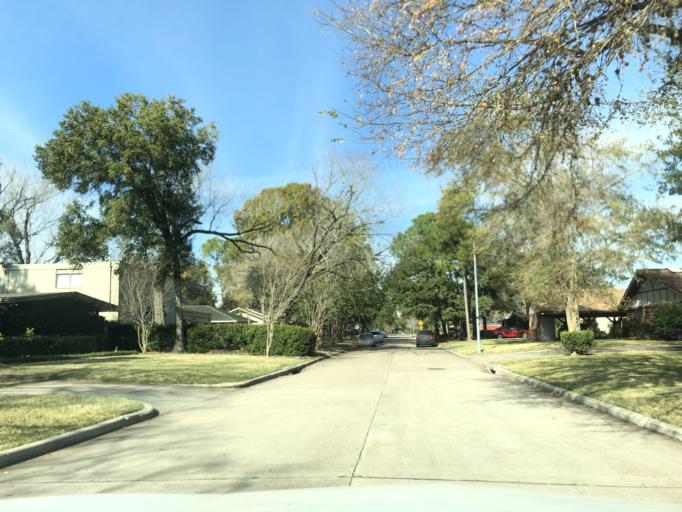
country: US
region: Texas
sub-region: Harris County
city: Bellaire
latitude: 29.6774
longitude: -95.5108
